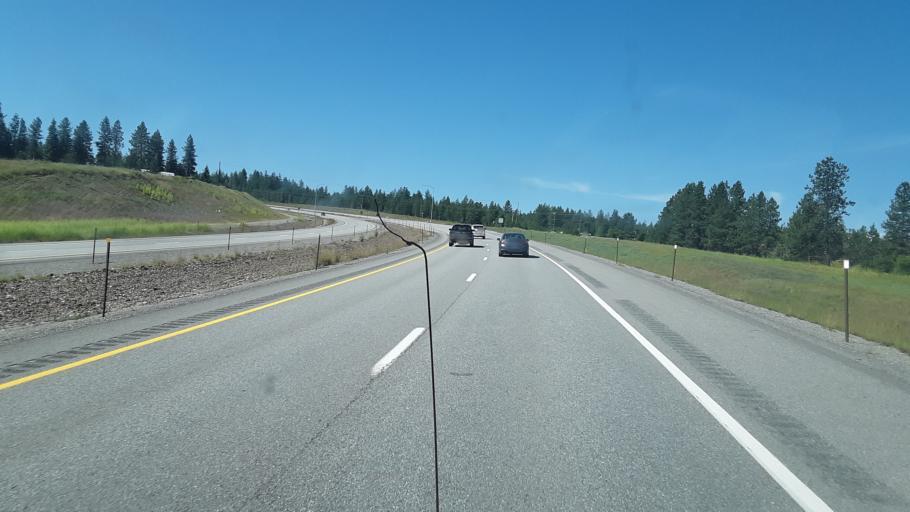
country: US
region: Idaho
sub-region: Kootenai County
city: Spirit Lake
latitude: 47.9887
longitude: -116.6945
